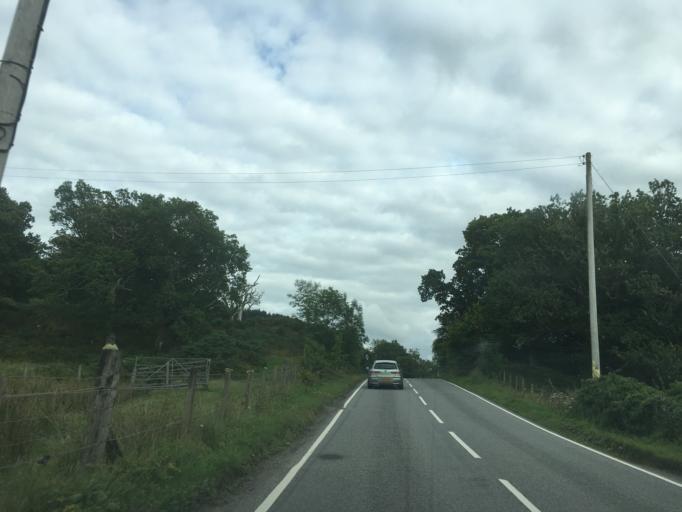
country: GB
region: Scotland
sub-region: Argyll and Bute
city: Oban
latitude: 56.3311
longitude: -5.5099
